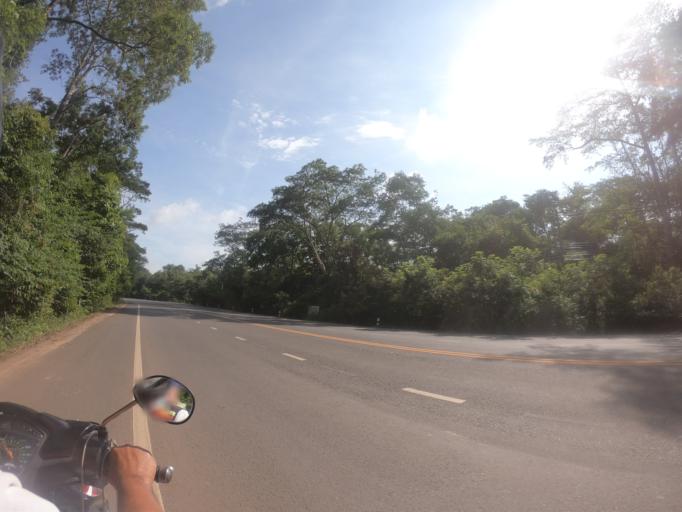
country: TH
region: Surin
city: Kap Choeng
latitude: 14.4471
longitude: 103.7006
